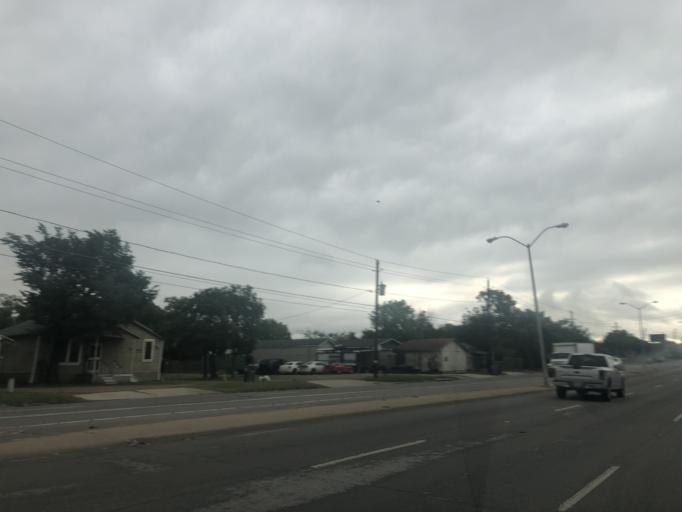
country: US
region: Texas
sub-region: Dallas County
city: Cockrell Hill
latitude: 32.7788
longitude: -96.8807
